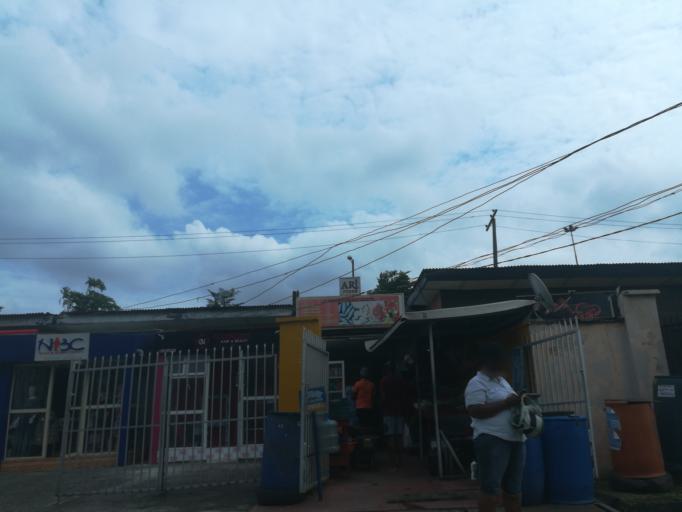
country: NG
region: Lagos
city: Somolu
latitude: 6.5473
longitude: 3.3829
